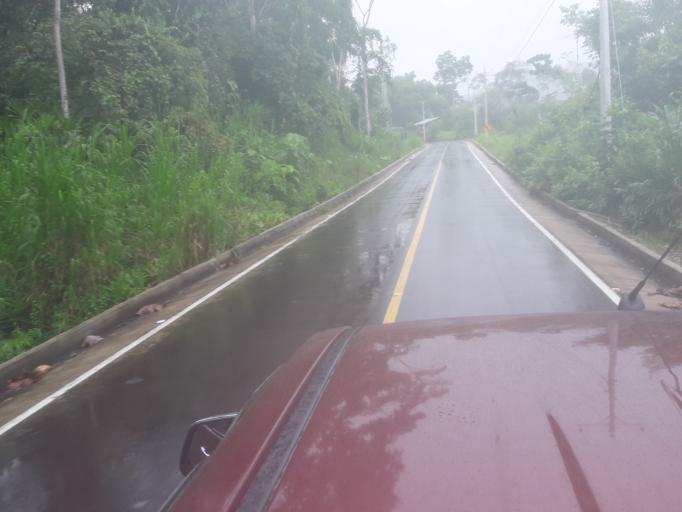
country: EC
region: Napo
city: Tena
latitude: -1.0241
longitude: -77.6658
